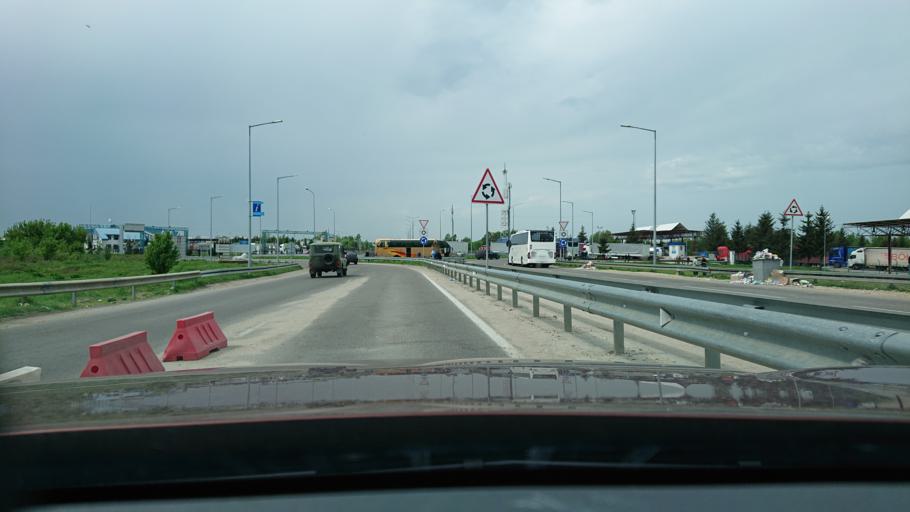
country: PL
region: Subcarpathian Voivodeship
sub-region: Powiat lubaczowski
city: Wielkie Oczy
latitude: 49.9563
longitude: 23.1235
